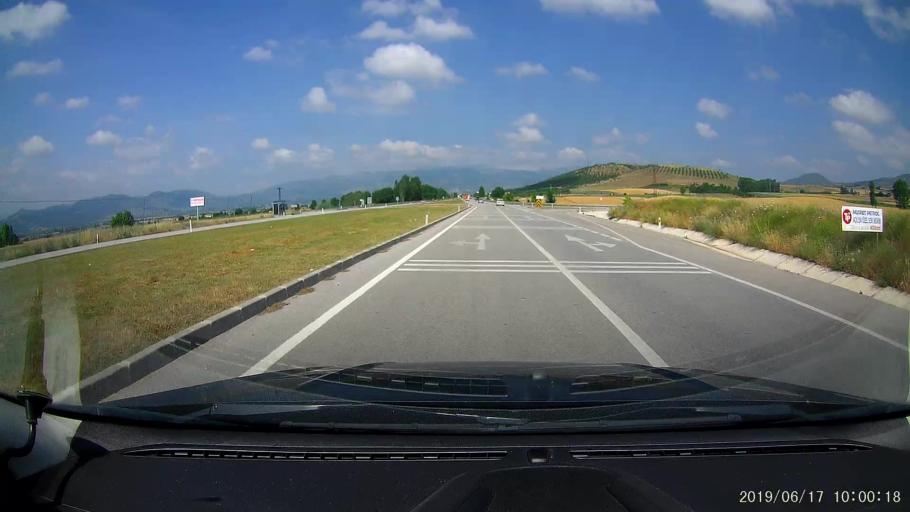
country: TR
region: Amasya
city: Alicik
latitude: 40.8664
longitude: 35.2914
